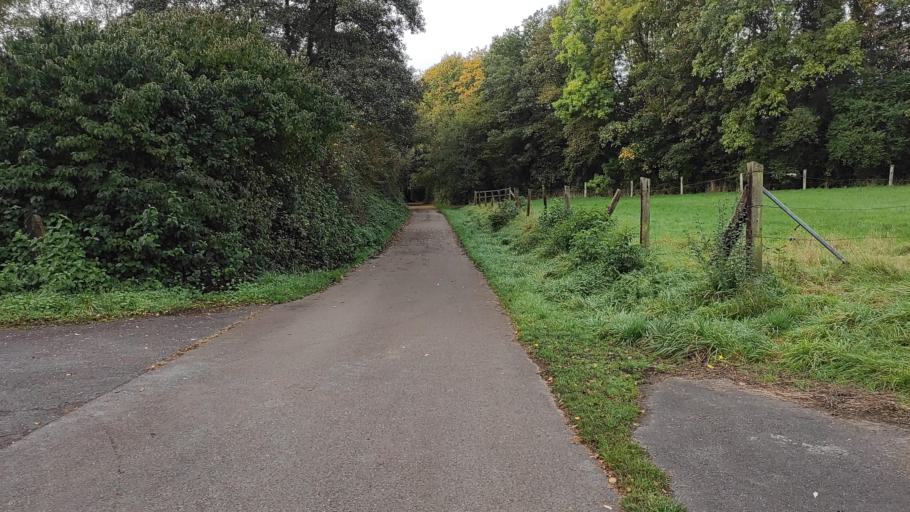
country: DE
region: North Rhine-Westphalia
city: Sprockhovel
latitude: 51.4127
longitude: 7.2625
